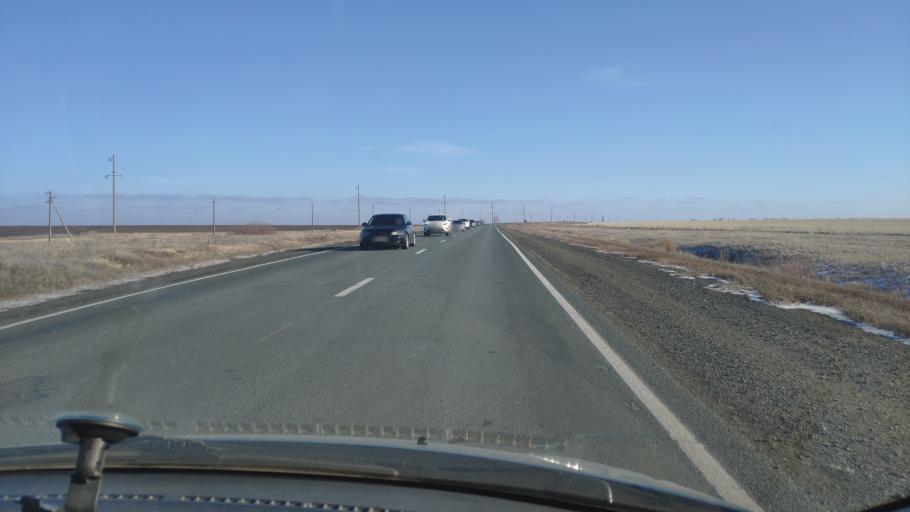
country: RU
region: Orenburg
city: Mednogorsk
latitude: 51.4355
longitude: 57.8934
